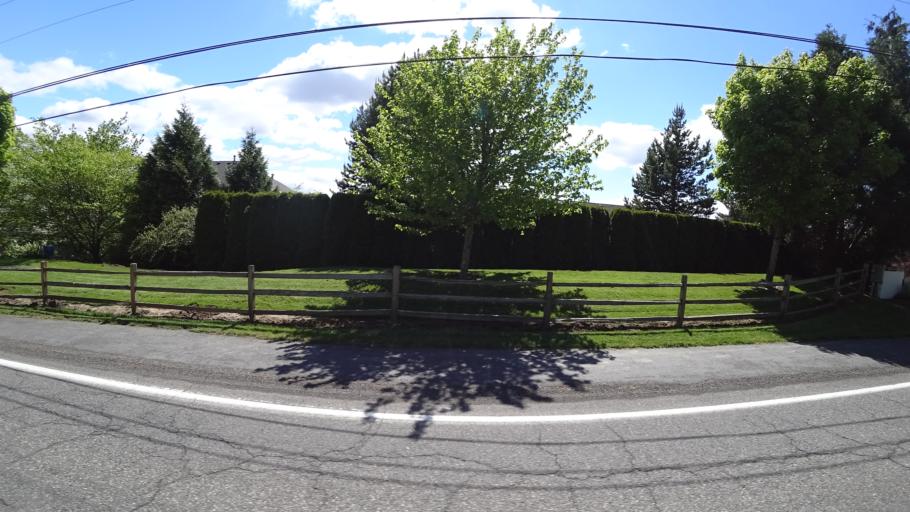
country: US
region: Oregon
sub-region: Washington County
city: West Haven
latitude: 45.5516
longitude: -122.7720
